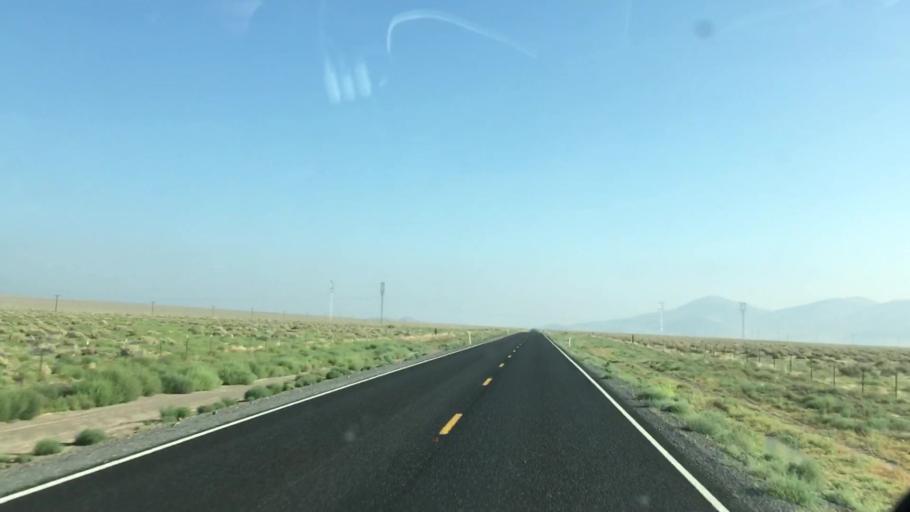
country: US
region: Nevada
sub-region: Lyon County
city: Fernley
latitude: 39.6986
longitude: -119.3349
